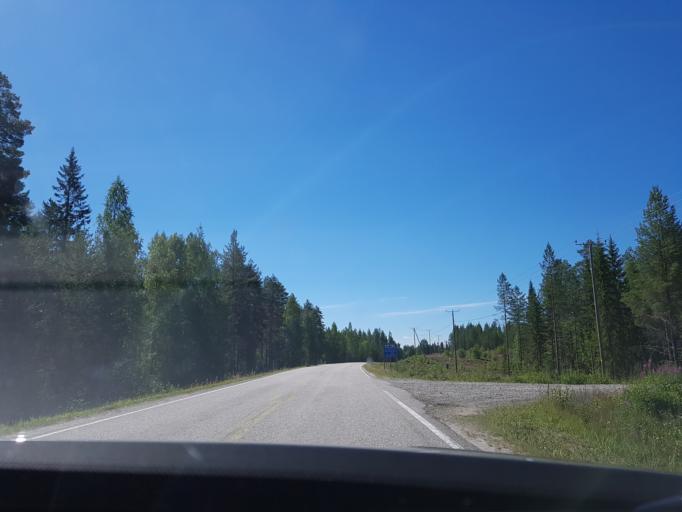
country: FI
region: Kainuu
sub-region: Kehys-Kainuu
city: Kuhmo
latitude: 64.1727
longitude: 29.6590
